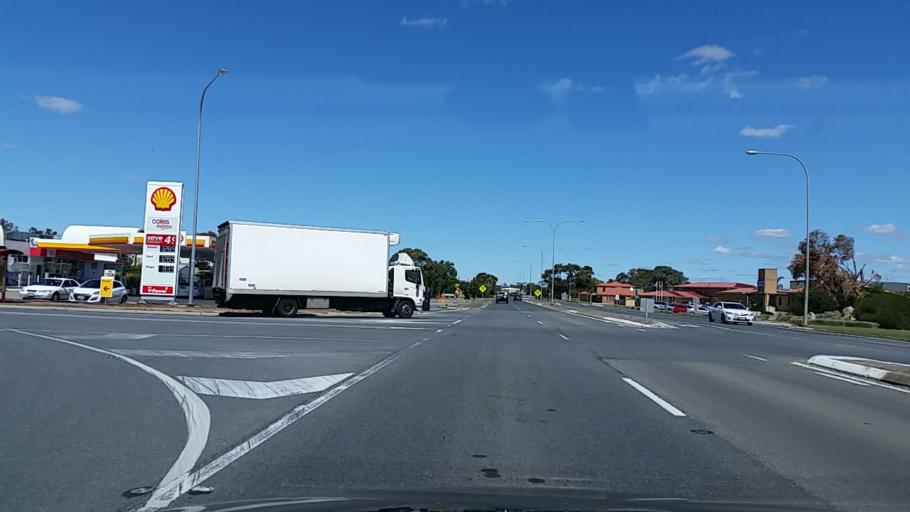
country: AU
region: South Australia
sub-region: Murray Bridge
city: Tailem Bend
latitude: -35.2534
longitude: 139.4522
